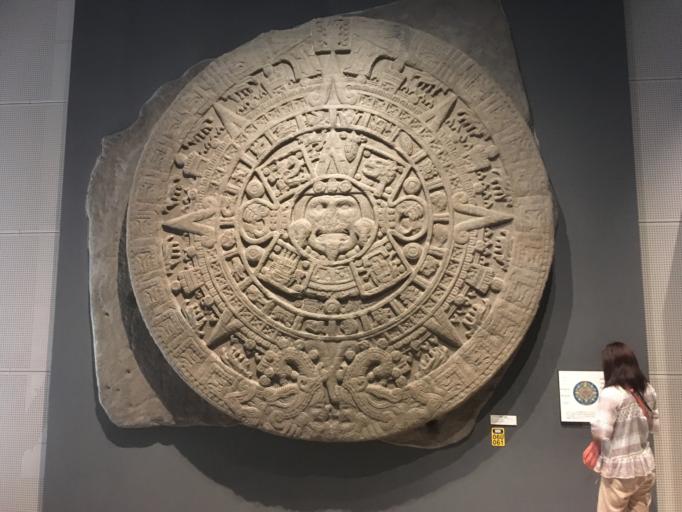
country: JP
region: Osaka
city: Ibaraki
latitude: 34.8124
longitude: 135.5298
